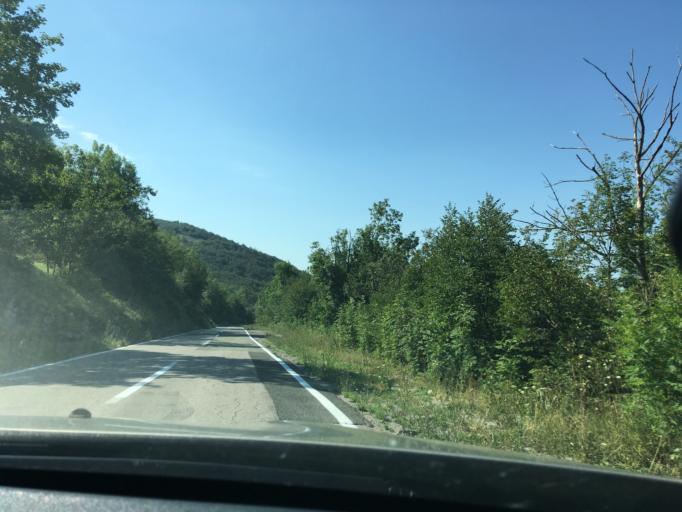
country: HR
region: Primorsko-Goranska
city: Hreljin
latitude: 45.3571
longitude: 14.6171
